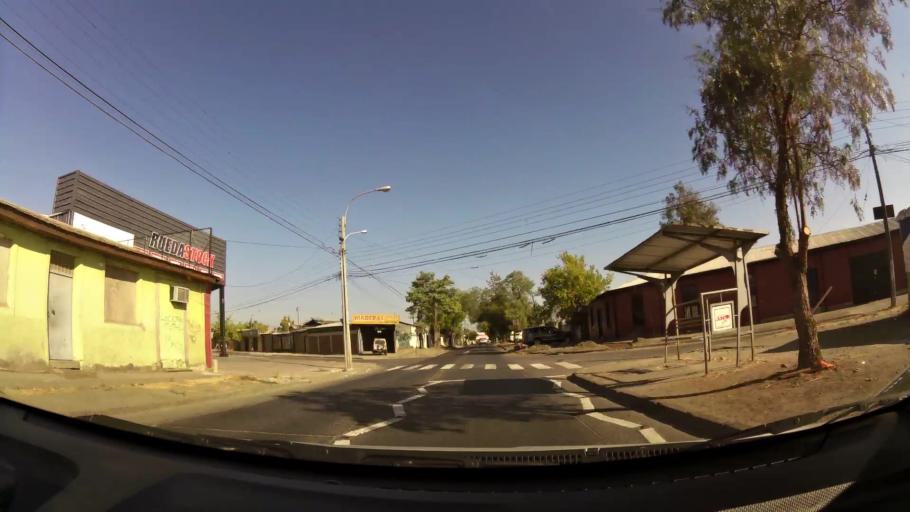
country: CL
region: Maule
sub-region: Provincia de Talca
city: Talca
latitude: -35.4199
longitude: -71.6518
